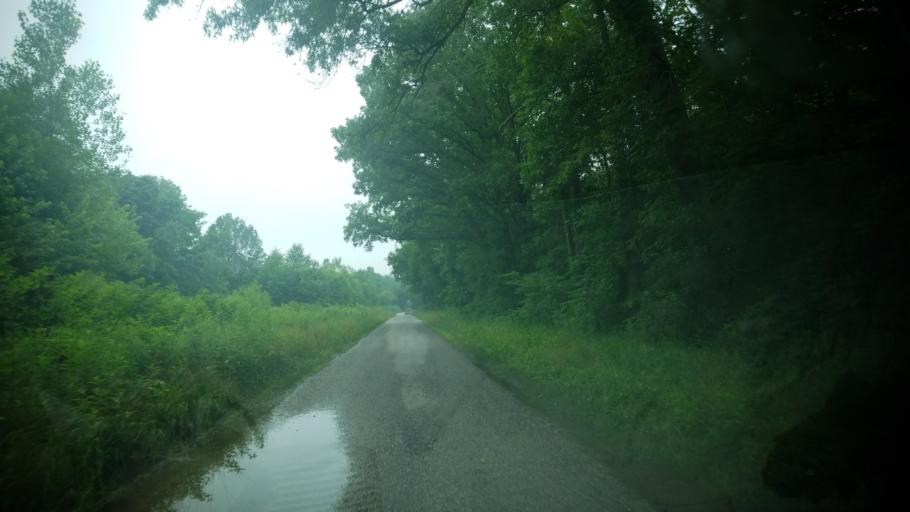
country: US
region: Illinois
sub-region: Clay County
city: Flora
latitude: 38.5734
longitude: -88.3703
